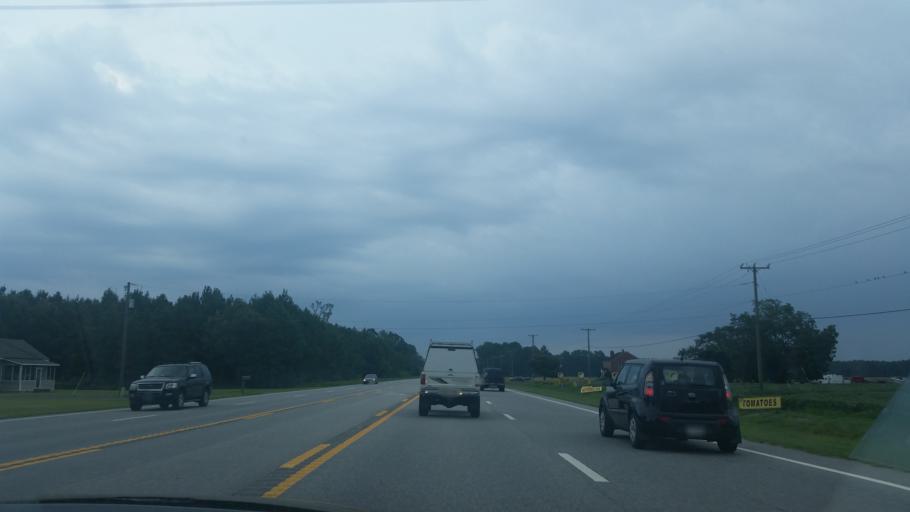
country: US
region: North Carolina
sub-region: Currituck County
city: Currituck
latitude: 36.4581
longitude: -76.0947
